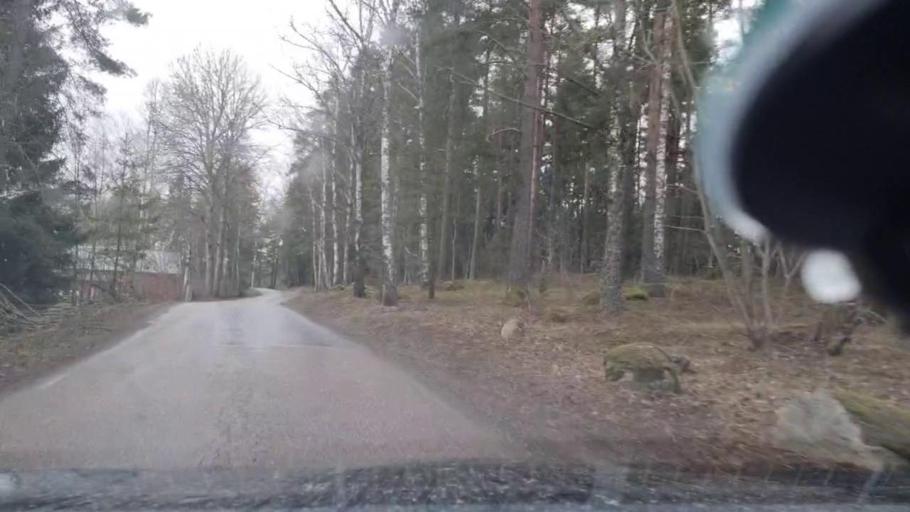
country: SE
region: Stockholm
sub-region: Taby Kommun
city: Taby
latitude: 59.4901
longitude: 18.0056
